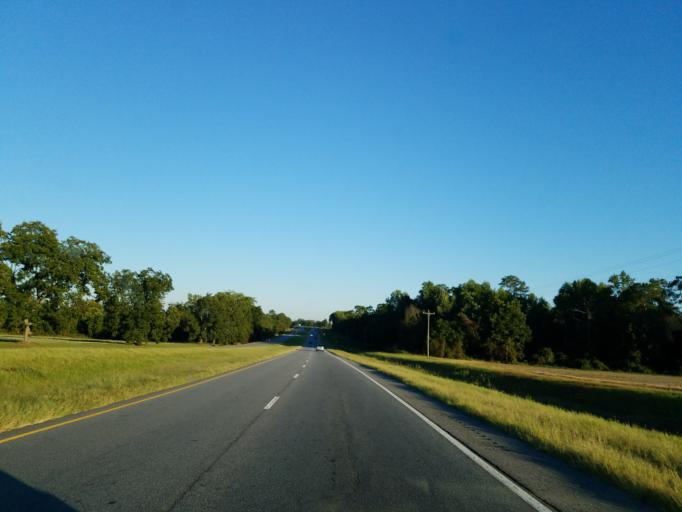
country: US
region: Georgia
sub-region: Worth County
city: Sylvester
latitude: 31.4874
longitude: -83.7023
